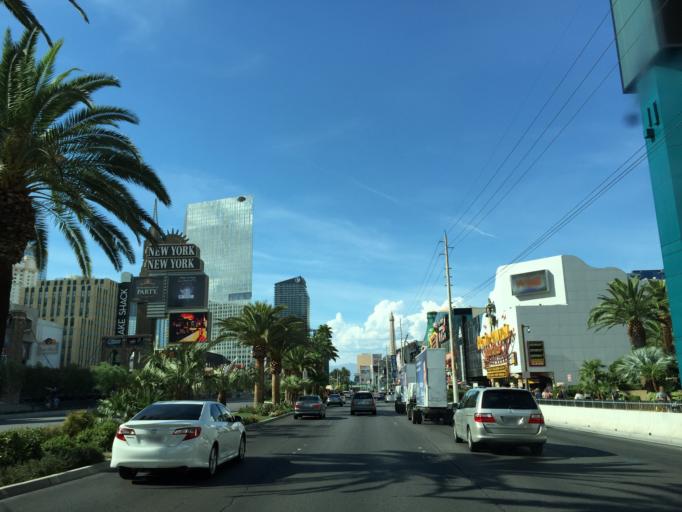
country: US
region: Nevada
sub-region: Clark County
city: Paradise
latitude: 36.1015
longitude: -115.1728
